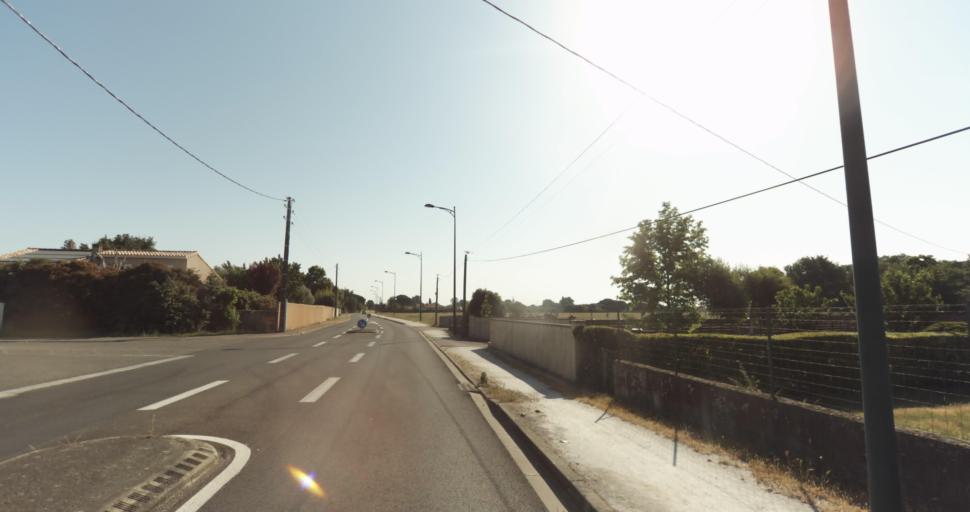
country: FR
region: Midi-Pyrenees
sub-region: Departement de la Haute-Garonne
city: La Salvetat-Saint-Gilles
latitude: 43.5648
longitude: 1.2700
